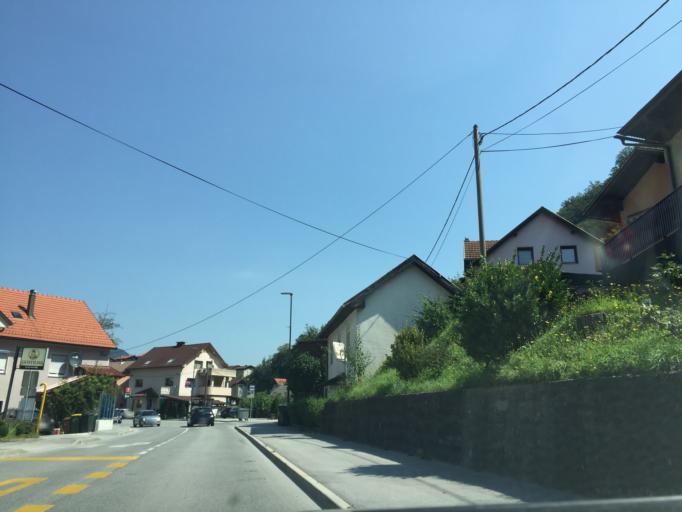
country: SI
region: Zagorje ob Savi
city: Zagorje ob Savi
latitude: 46.1273
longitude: 14.9971
